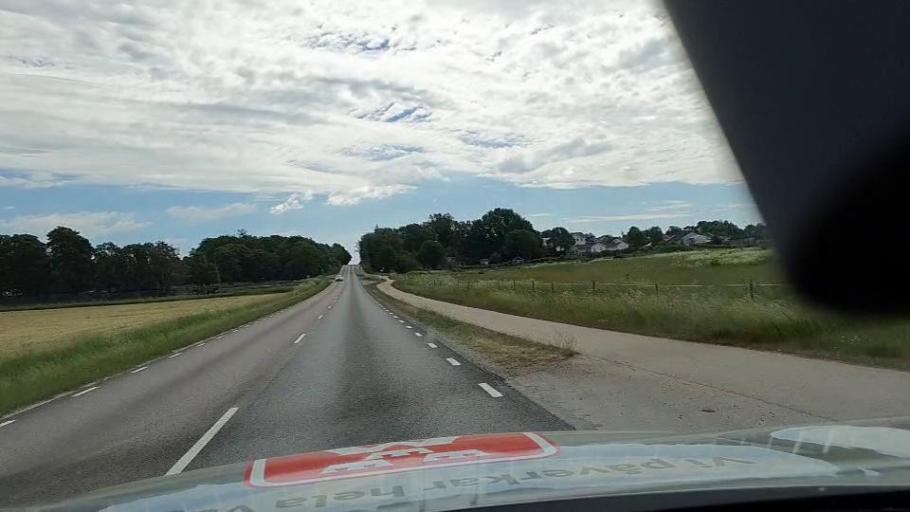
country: SE
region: Blekinge
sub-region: Karlskrona Kommun
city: Jaemjoe
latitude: 56.1726
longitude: 15.7292
